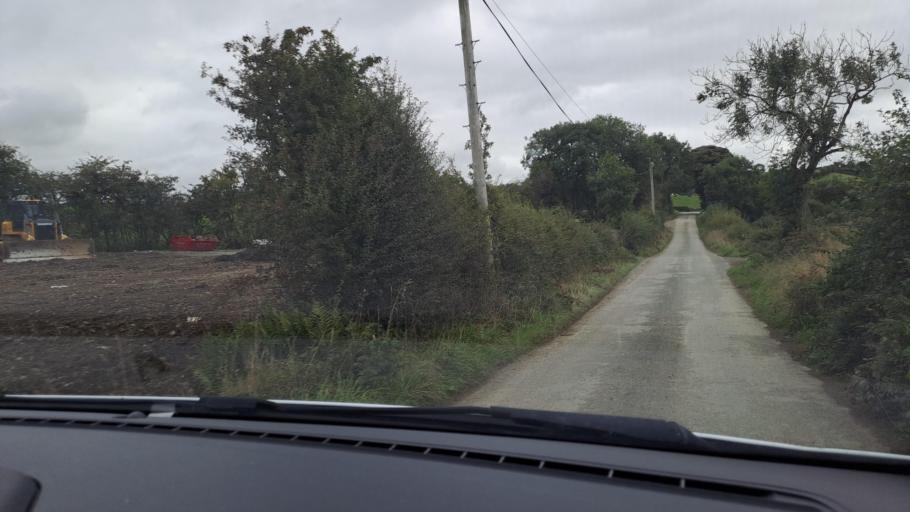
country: IE
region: Ulster
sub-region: County Monaghan
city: Castleblayney
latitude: 54.0418
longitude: -6.7948
